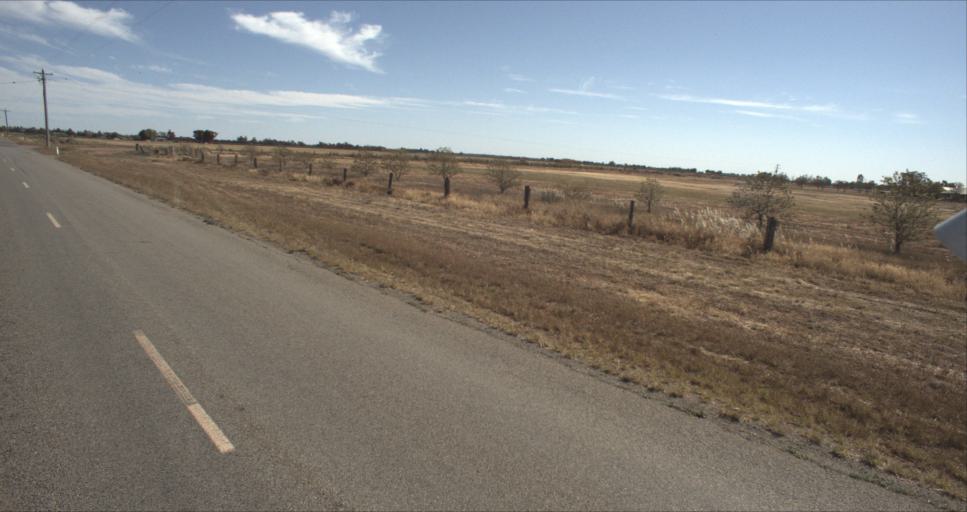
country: AU
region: New South Wales
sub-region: Leeton
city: Leeton
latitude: -34.5709
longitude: 146.3817
